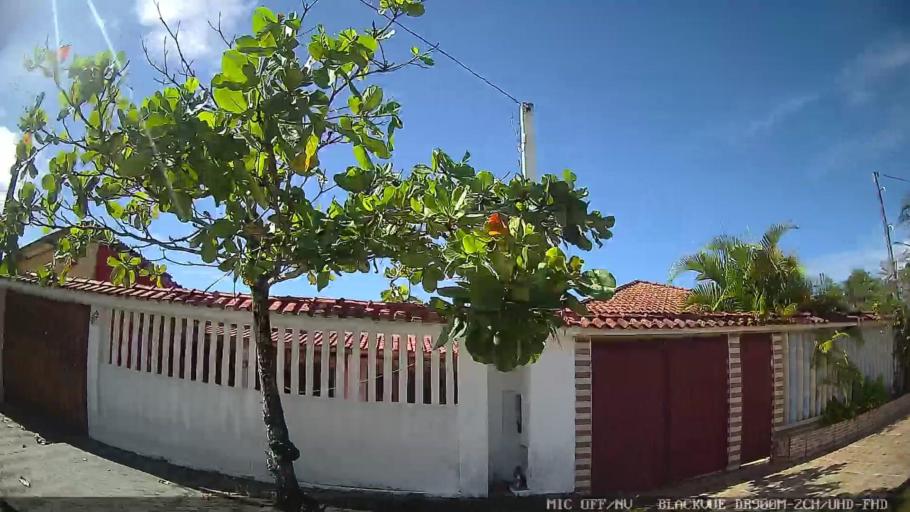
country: BR
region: Sao Paulo
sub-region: Itanhaem
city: Itanhaem
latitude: -24.2396
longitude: -46.8981
